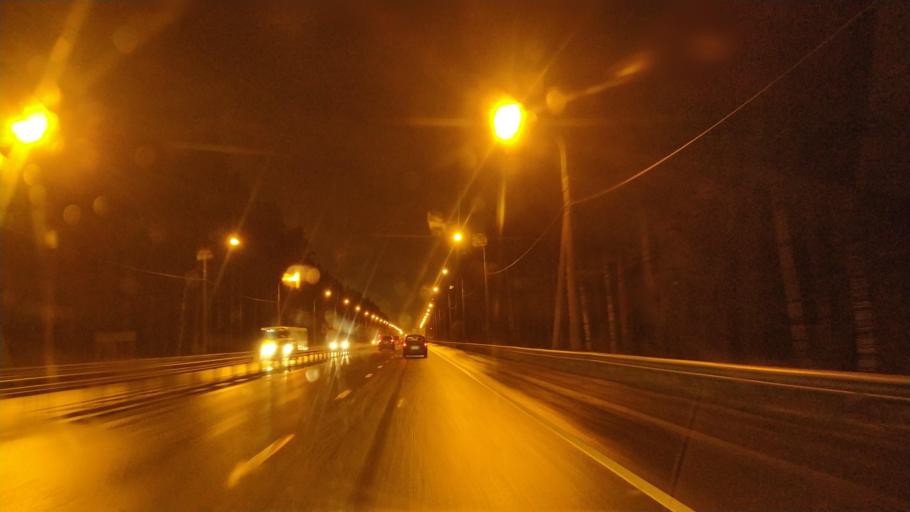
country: RU
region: St.-Petersburg
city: Krasnogvargeisky
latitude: 60.0002
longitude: 30.5529
